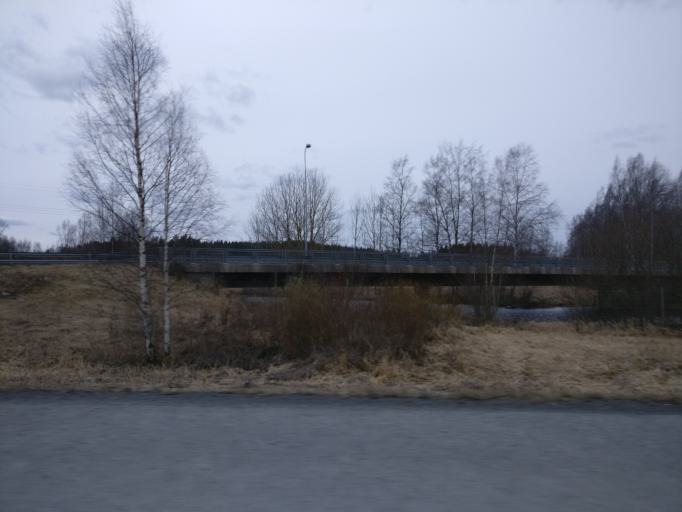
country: FI
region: Pirkanmaa
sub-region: Etelae-Pirkanmaa
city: Toijala
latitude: 61.2024
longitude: 23.8422
